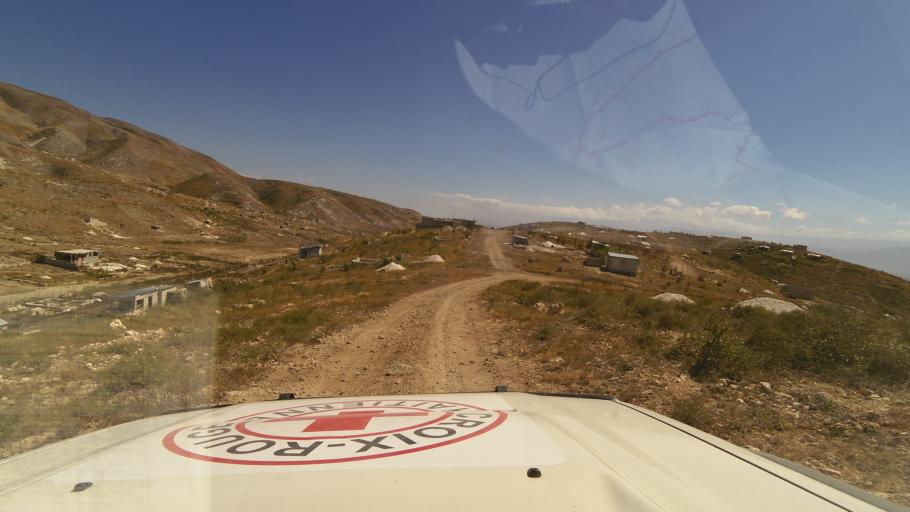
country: HT
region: Ouest
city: Croix des Bouquets
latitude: 18.6766
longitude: -72.2942
